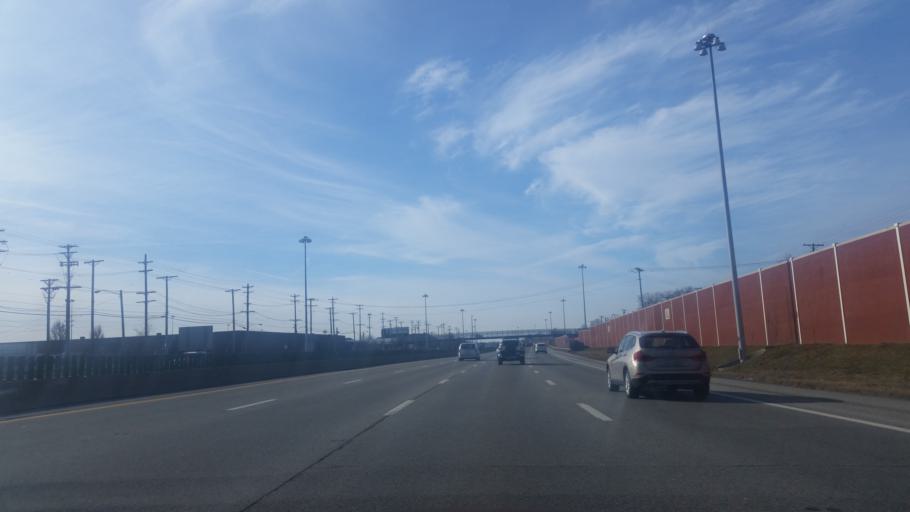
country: US
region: Ohio
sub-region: Cuyahoga County
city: Euclid
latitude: 41.5733
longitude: -81.5595
